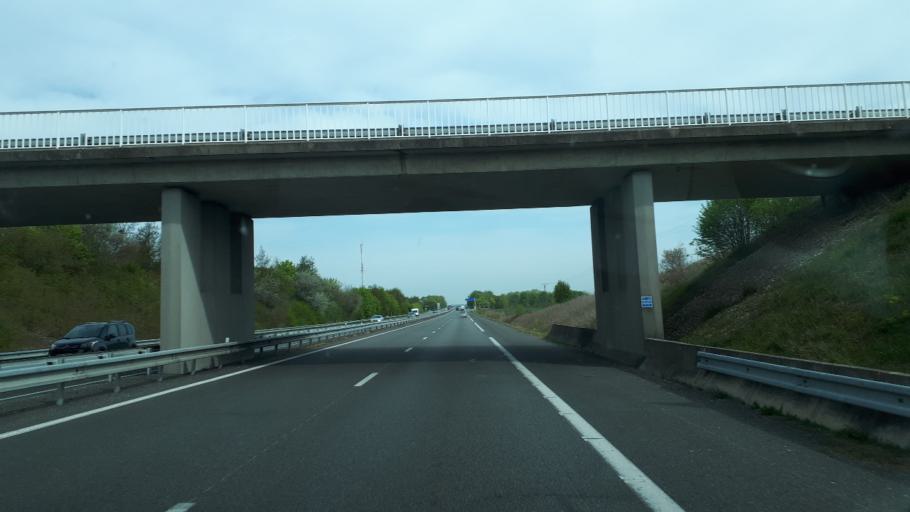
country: FR
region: Centre
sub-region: Departement du Cher
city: Mehun-sur-Yevre
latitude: 47.1376
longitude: 2.1871
